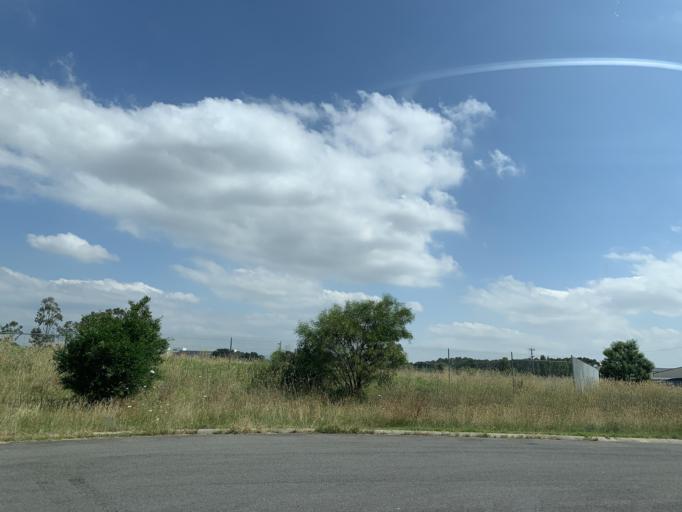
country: AU
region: Victoria
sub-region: Latrobe
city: Traralgon
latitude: -38.2133
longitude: 146.4706
